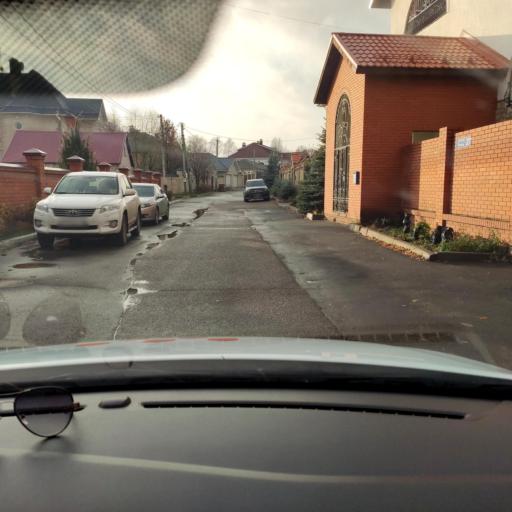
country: RU
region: Tatarstan
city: Stolbishchi
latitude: 55.7446
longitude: 49.2423
